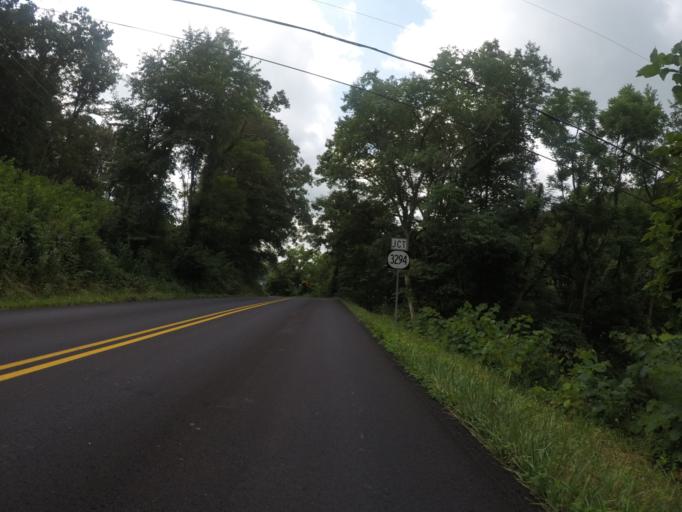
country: US
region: Kentucky
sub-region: Boyd County
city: Meads
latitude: 38.4011
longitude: -82.6569
